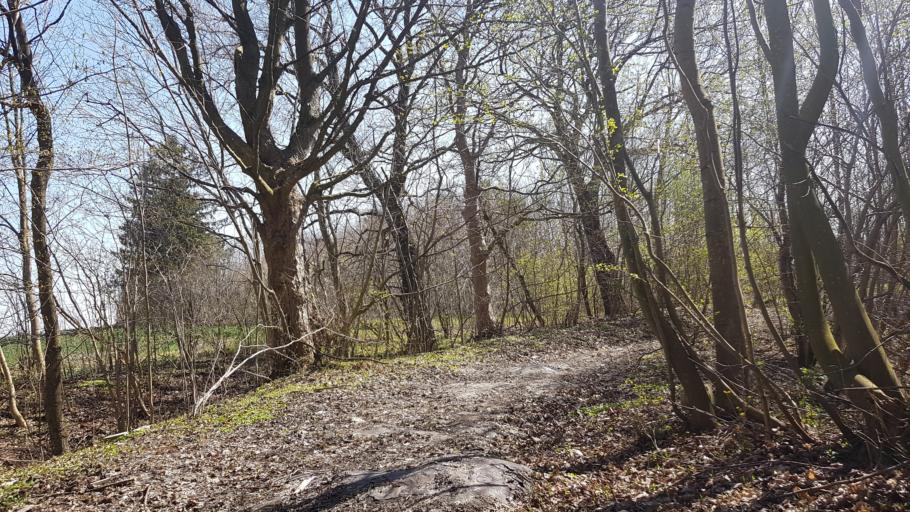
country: PL
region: Pomeranian Voivodeship
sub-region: Powiat slupski
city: Ustka
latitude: 54.5154
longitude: 16.7353
